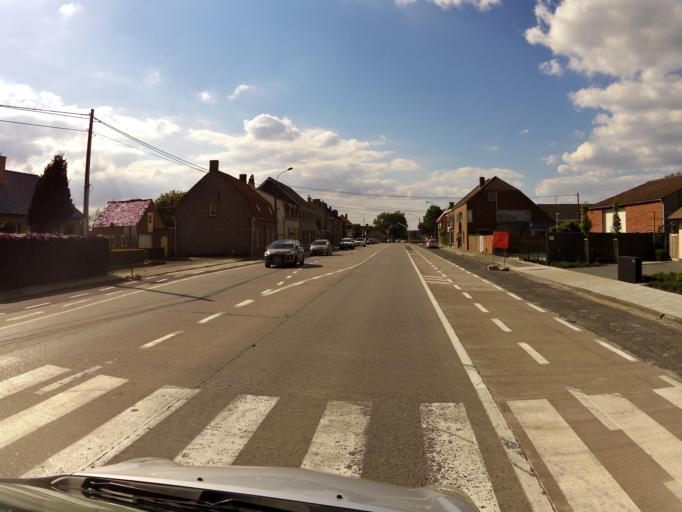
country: BE
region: Flanders
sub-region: Provincie West-Vlaanderen
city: Poperinge
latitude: 50.9304
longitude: 2.7390
